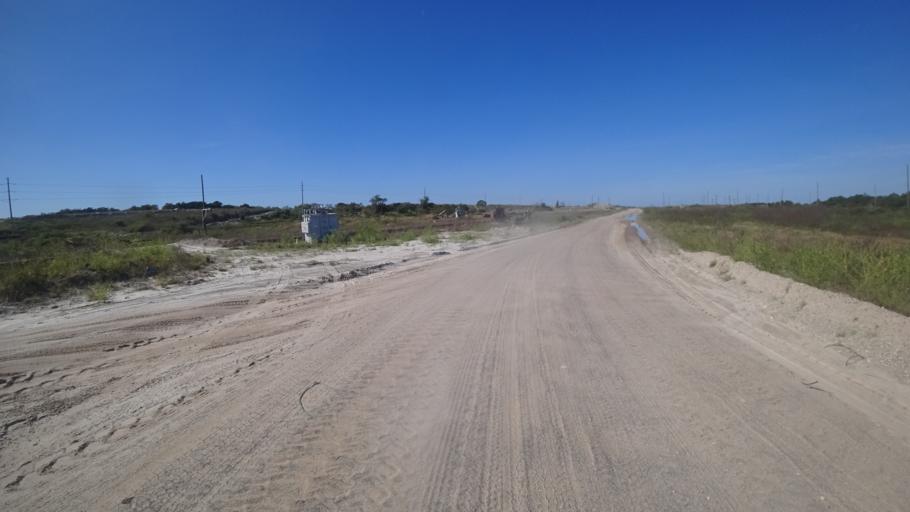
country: US
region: Florida
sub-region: Hillsborough County
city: Balm
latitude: 27.6474
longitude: -82.1064
